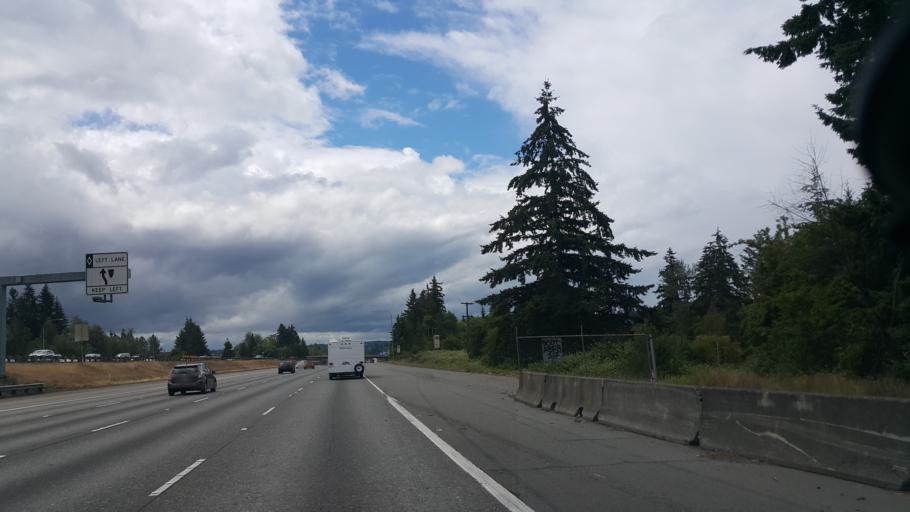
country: US
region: Washington
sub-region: Pierce County
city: Milton
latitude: 47.2702
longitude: -122.3174
